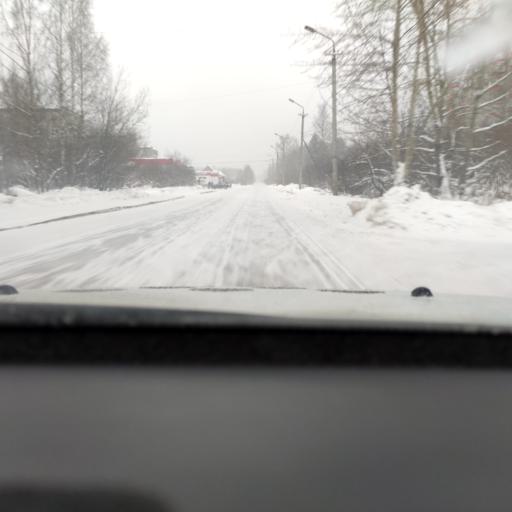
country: RU
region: Perm
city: Polazna
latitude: 58.1470
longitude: 56.4327
